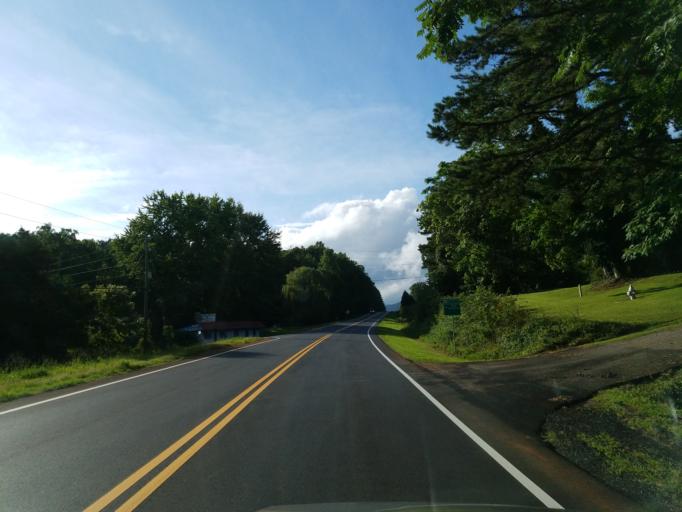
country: US
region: Georgia
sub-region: White County
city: Cleveland
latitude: 34.6395
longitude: -83.8348
